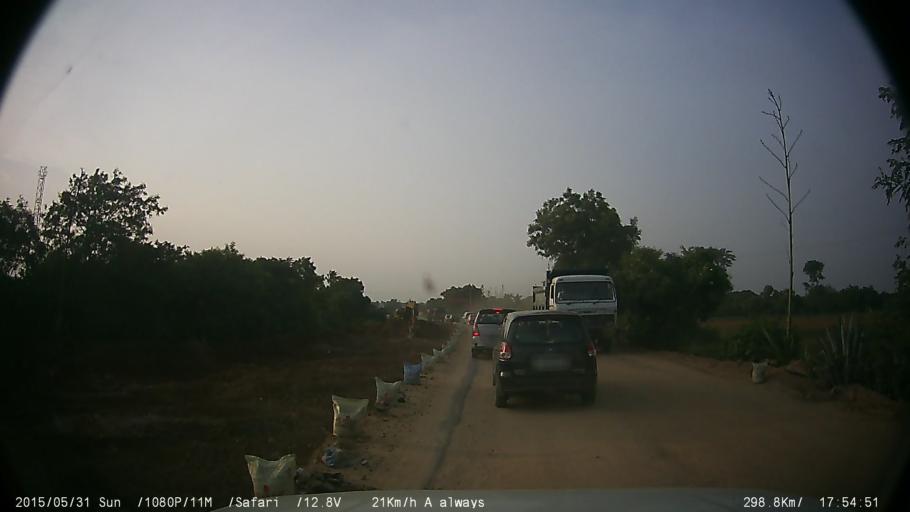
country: IN
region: Karnataka
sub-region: Mysore
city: Nanjangud
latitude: 11.9889
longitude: 76.6699
